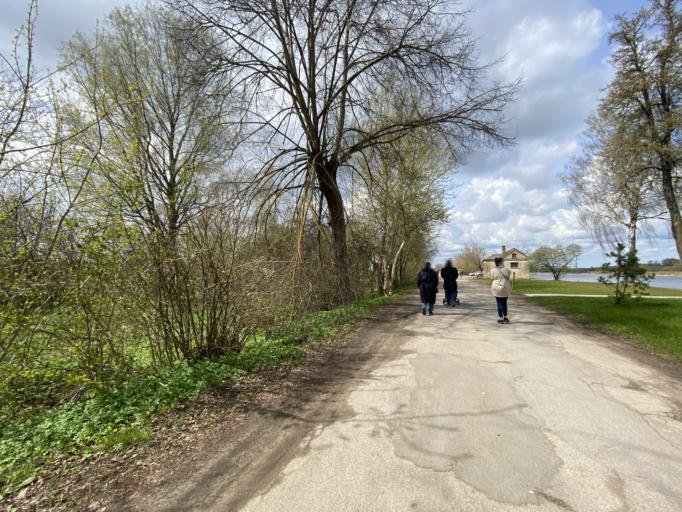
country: LV
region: Jelgava
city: Jelgava
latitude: 56.6597
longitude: 23.7304
